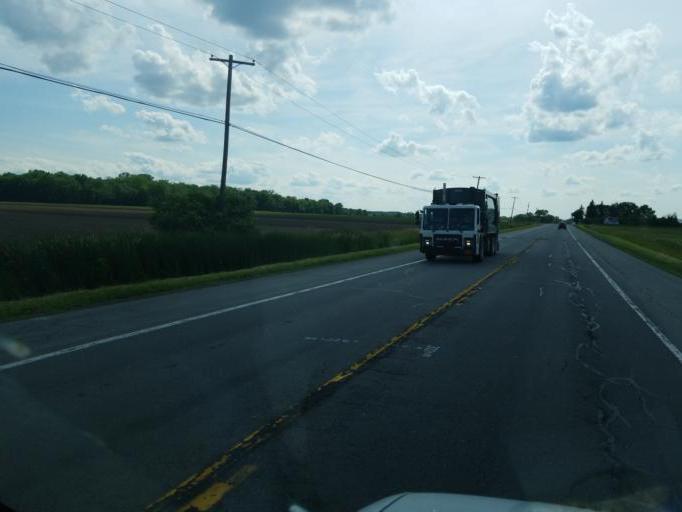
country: US
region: New York
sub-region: Ontario County
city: Clifton Springs
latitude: 42.8610
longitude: -77.1271
